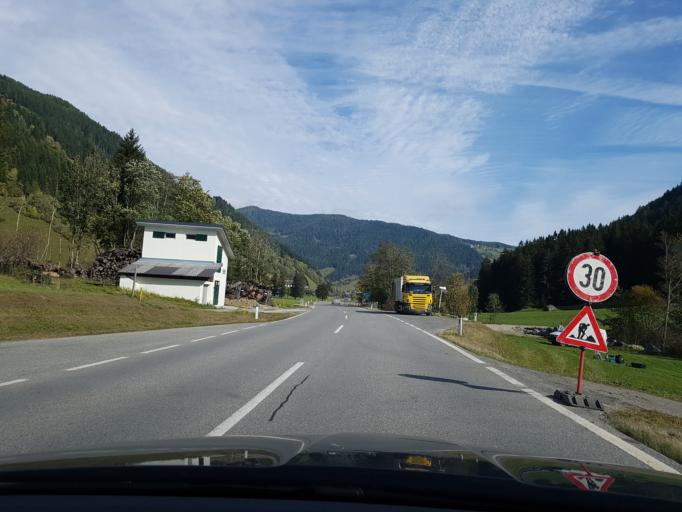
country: AT
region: Carinthia
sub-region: Politischer Bezirk Spittal an der Drau
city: Kleinkirchheim
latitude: 46.8386
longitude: 13.8743
